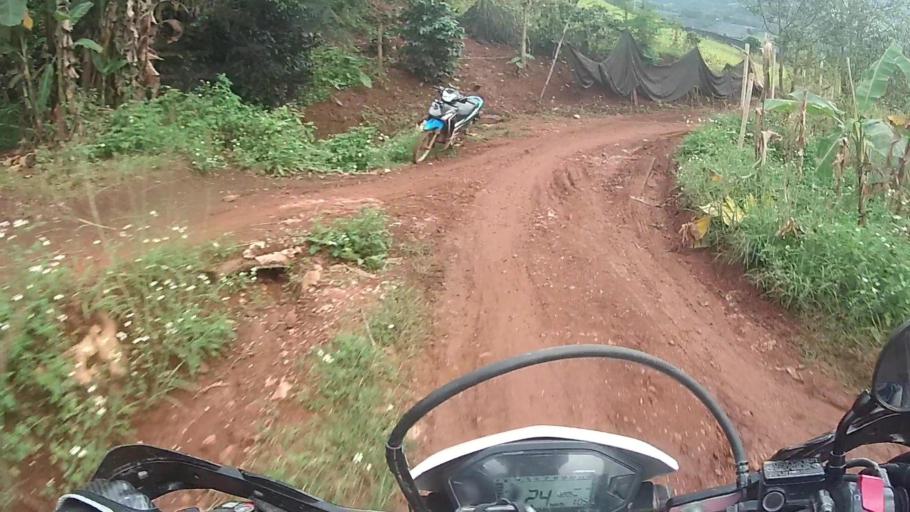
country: TH
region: Lampang
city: Wang Nuea
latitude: 19.0671
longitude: 99.4773
